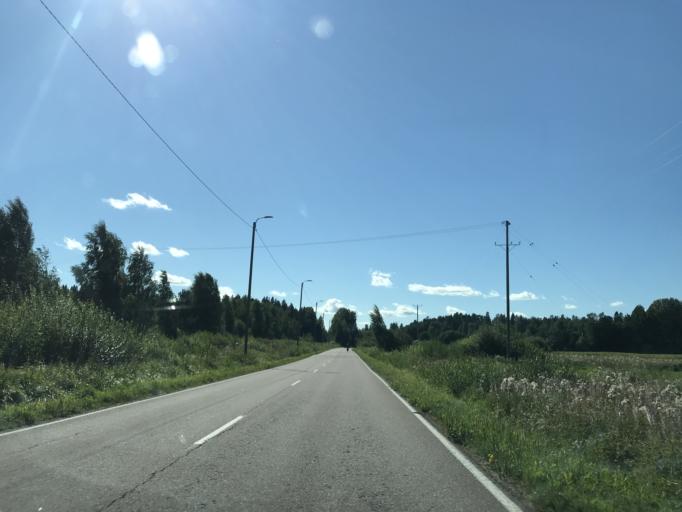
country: FI
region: Uusimaa
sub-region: Helsinki
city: Nurmijaervi
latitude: 60.4897
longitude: 24.6137
